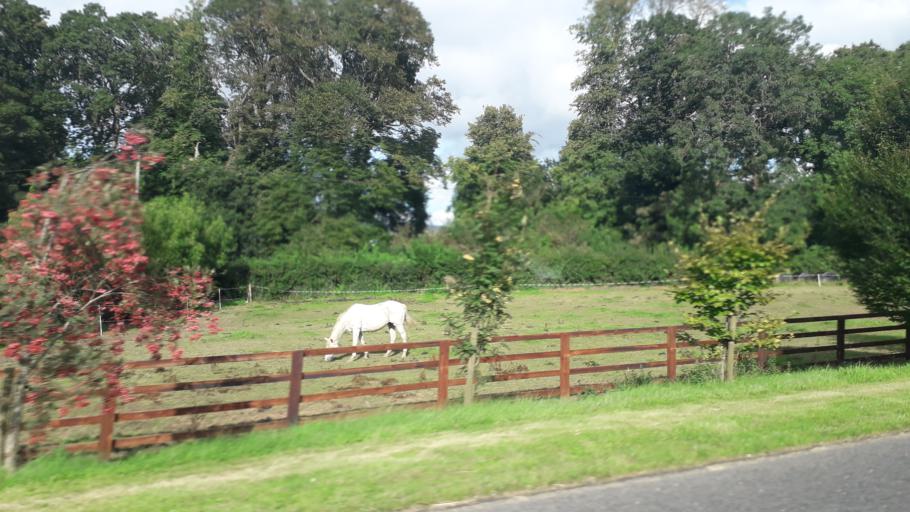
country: IE
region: Leinster
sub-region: Lu
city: Dundalk
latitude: 54.0332
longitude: -6.3620
